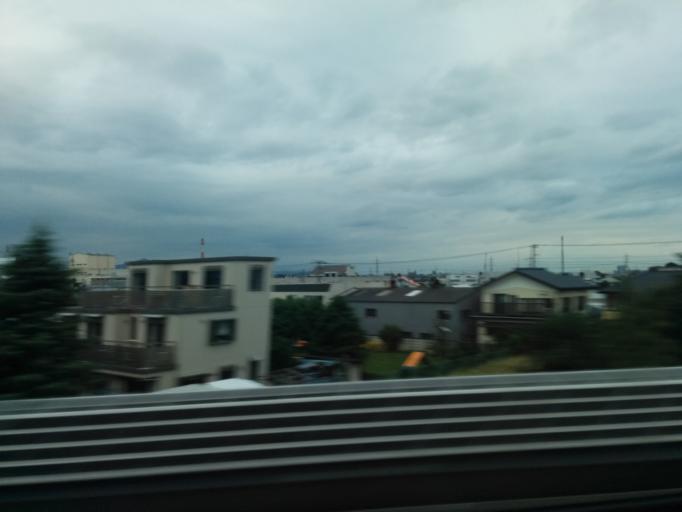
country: JP
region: Kanagawa
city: Atsugi
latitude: 35.3953
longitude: 139.3826
